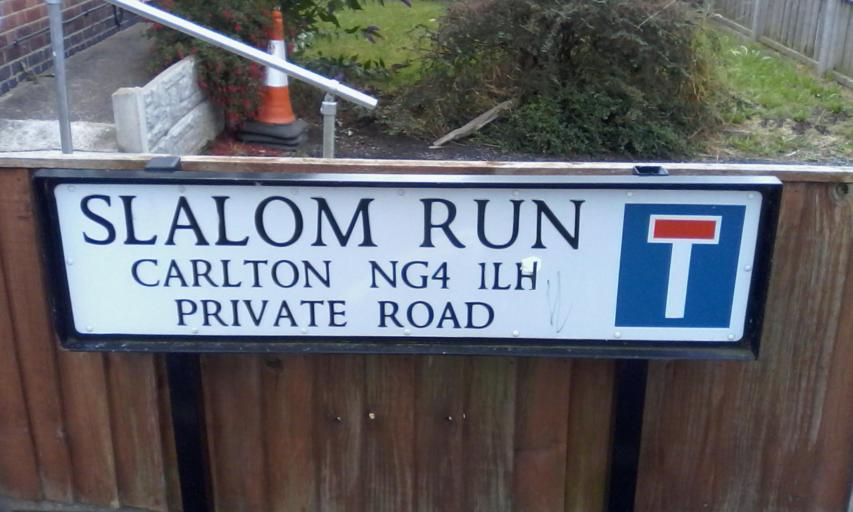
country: GB
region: England
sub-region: Nottinghamshire
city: Arnold
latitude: 52.9724
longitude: -1.1064
